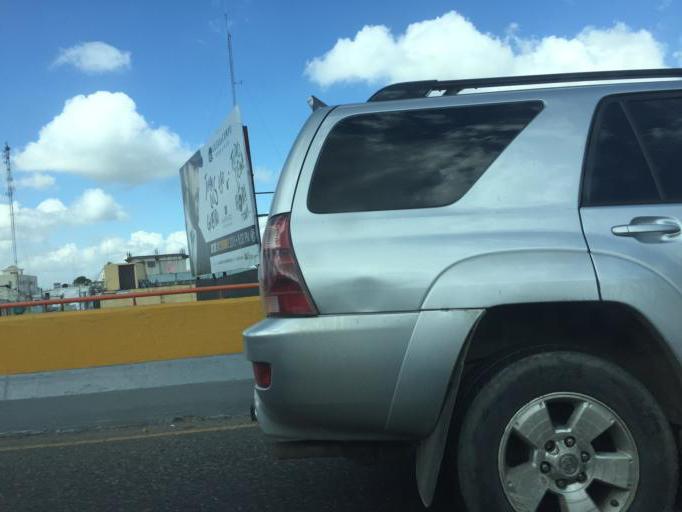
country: DO
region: Nacional
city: San Carlos
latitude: 18.4803
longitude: -69.8976
